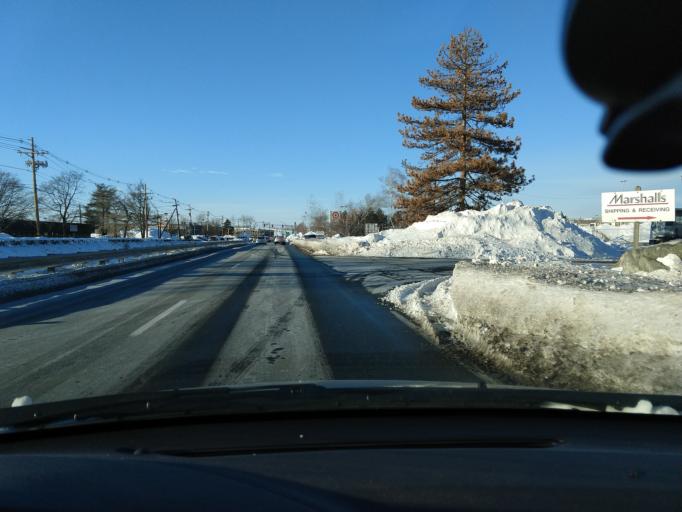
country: US
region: Massachusetts
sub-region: Middlesex County
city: Woburn
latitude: 42.5153
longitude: -71.1361
